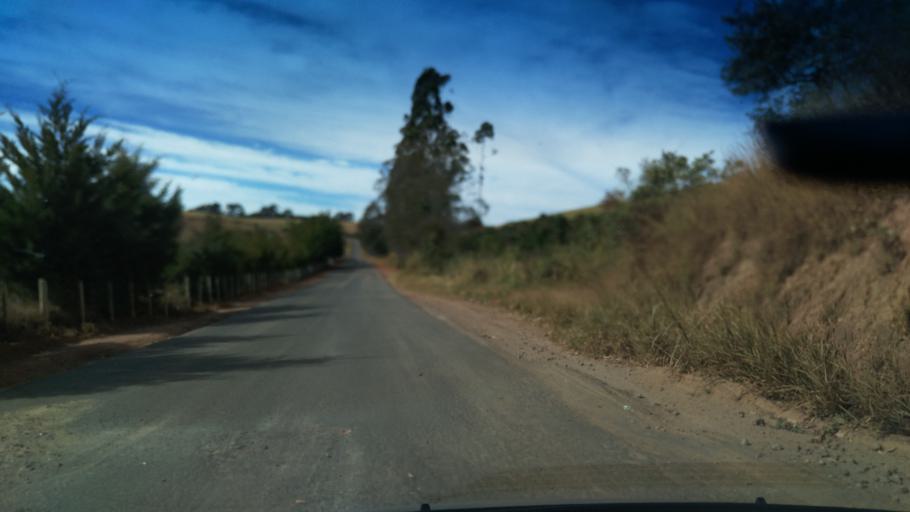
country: BR
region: Minas Gerais
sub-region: Andradas
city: Andradas
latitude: -22.0409
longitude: -46.3463
